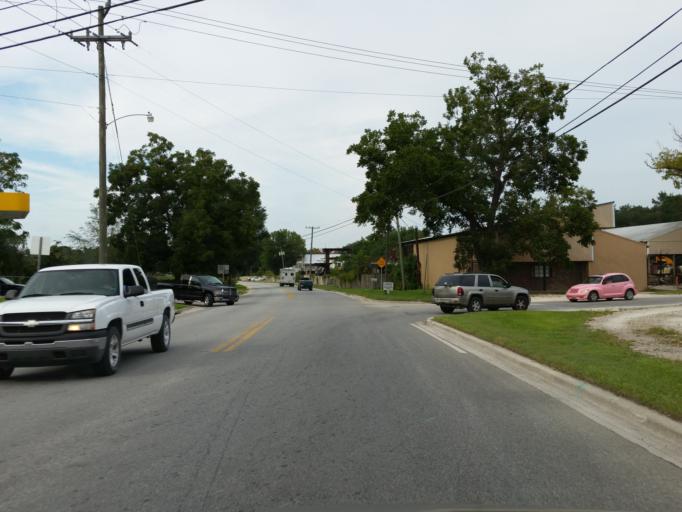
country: US
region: Florida
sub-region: Suwannee County
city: Live Oak
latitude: 30.3046
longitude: -82.9849
